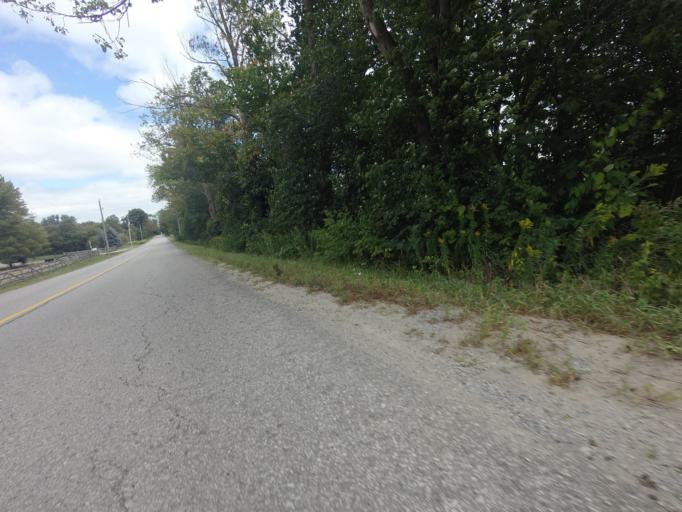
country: CA
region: Ontario
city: Uxbridge
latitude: 44.1224
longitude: -79.1475
